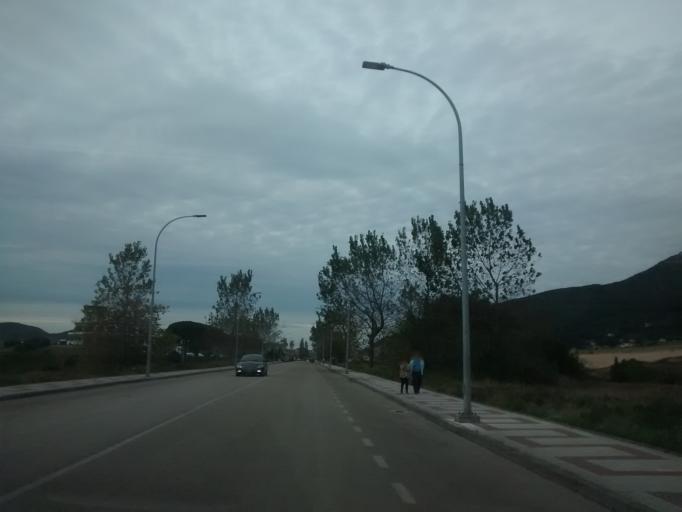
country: ES
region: Cantabria
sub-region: Provincia de Cantabria
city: Santona
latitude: 43.4295
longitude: -3.4488
